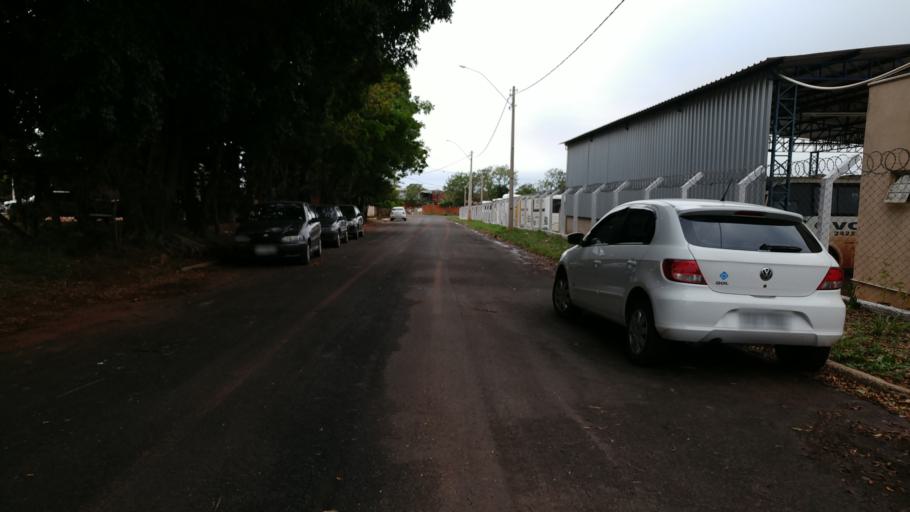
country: BR
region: Sao Paulo
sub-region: Paraguacu Paulista
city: Paraguacu Paulista
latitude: -22.4409
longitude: -50.5844
